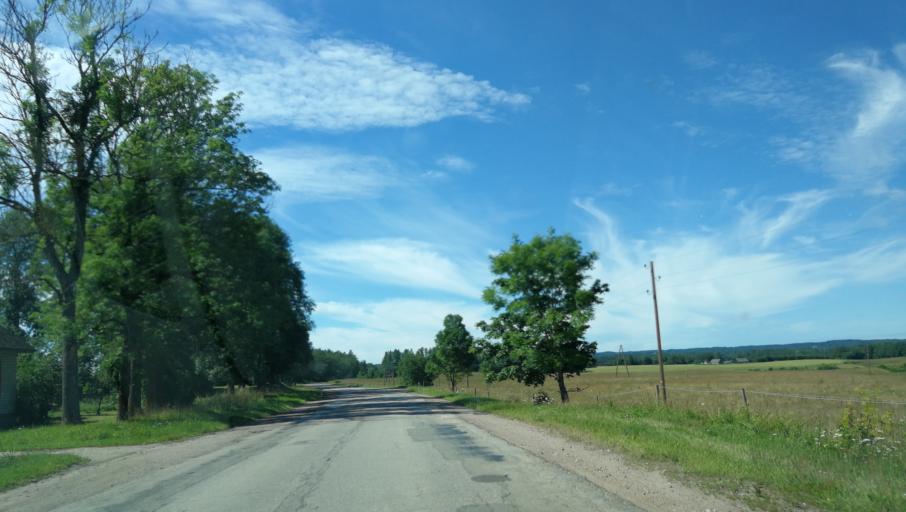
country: LV
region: Cesvaine
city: Cesvaine
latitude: 57.0053
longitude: 26.4036
